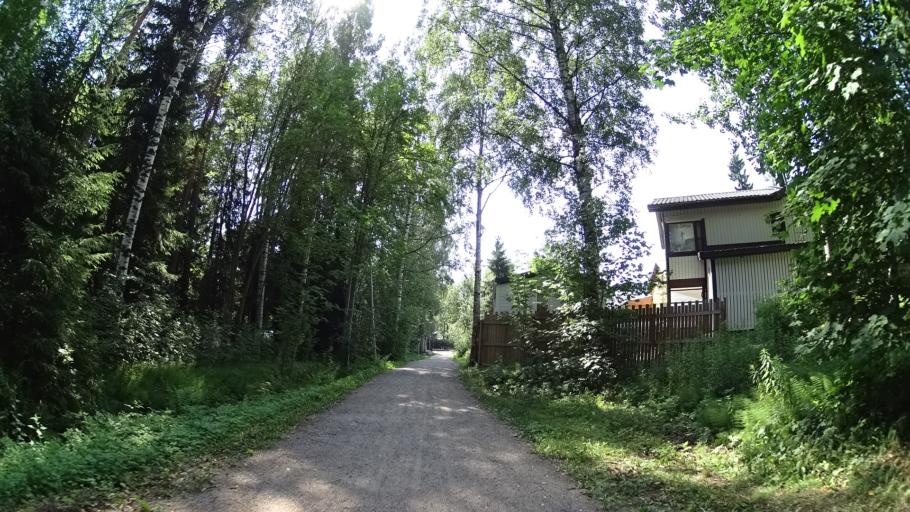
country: FI
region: Uusimaa
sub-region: Helsinki
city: Vantaa
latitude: 60.3314
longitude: 25.0520
